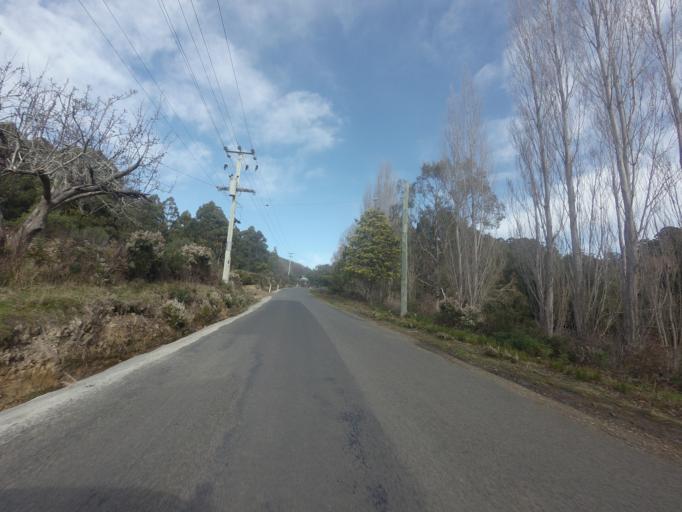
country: AU
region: Tasmania
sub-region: Kingborough
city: Margate
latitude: -42.9964
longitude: 147.1809
